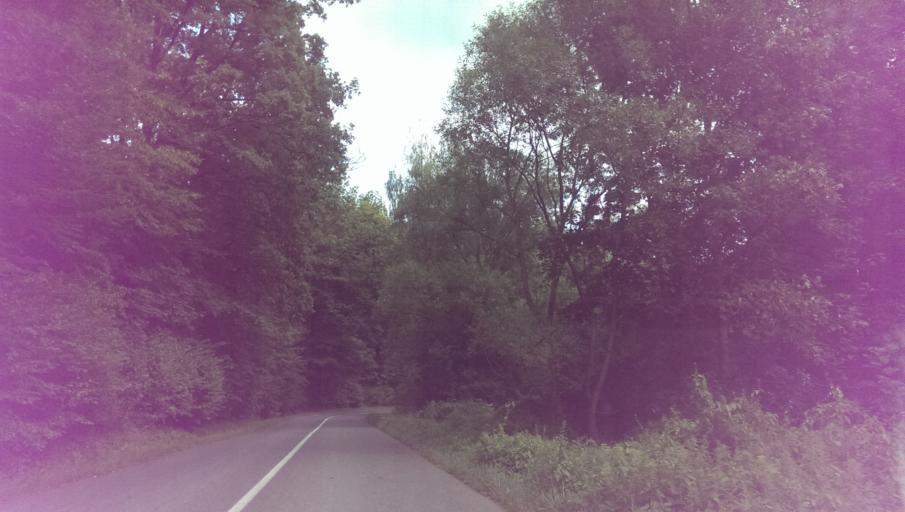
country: CZ
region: South Moravian
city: Velka nad Velickou
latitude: 48.8966
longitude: 17.5666
